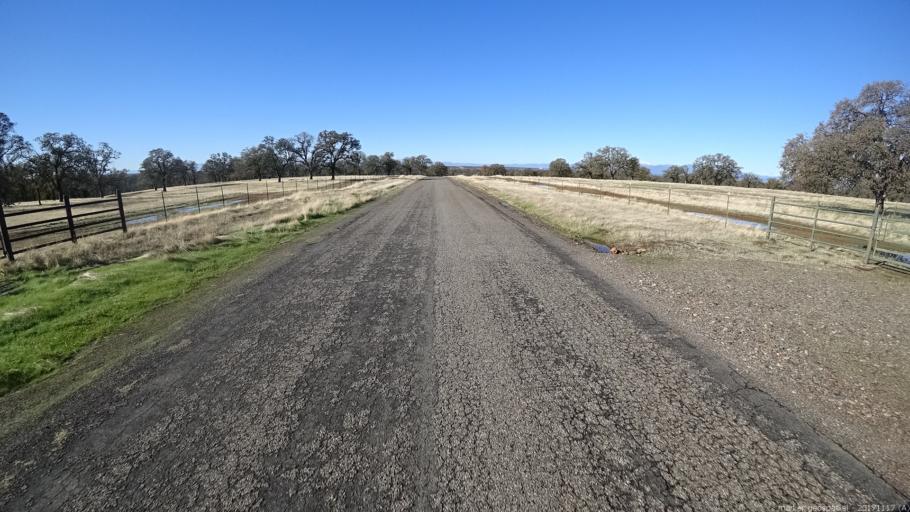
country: US
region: California
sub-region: Shasta County
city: Cottonwood
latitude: 40.4251
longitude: -122.1831
